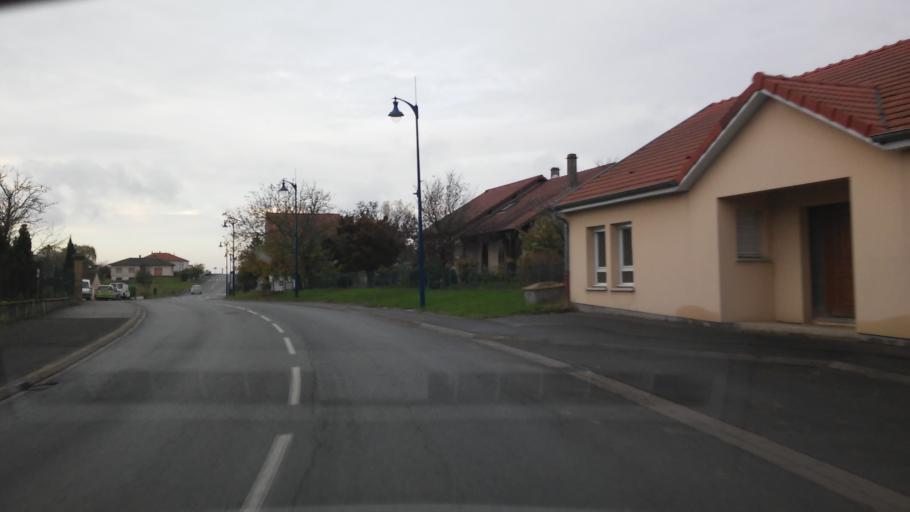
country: FR
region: Lorraine
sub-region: Departement de la Moselle
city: Ennery
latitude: 49.2088
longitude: 6.2349
